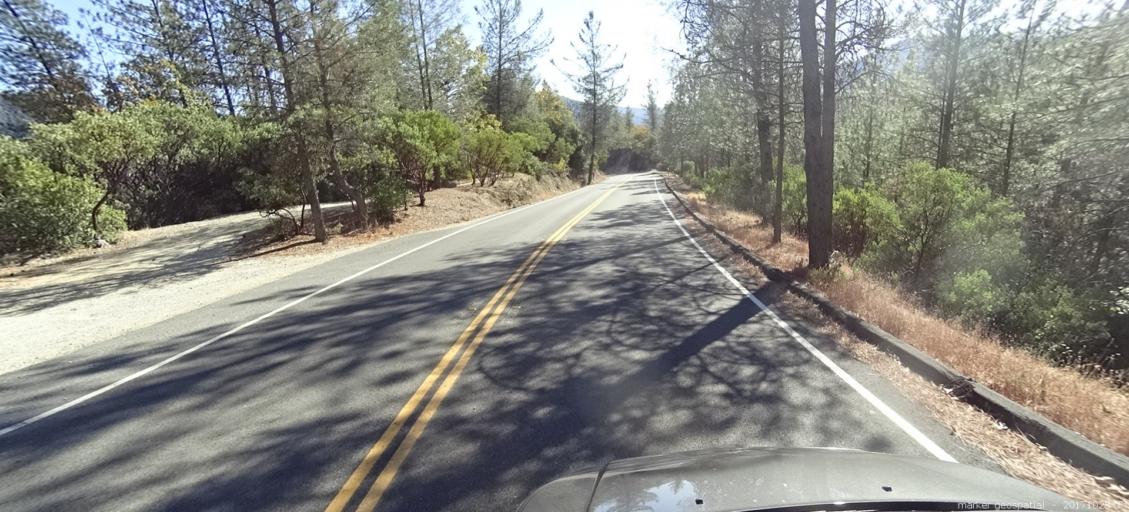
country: US
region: California
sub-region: Shasta County
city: Shasta
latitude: 40.6027
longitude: -122.5496
